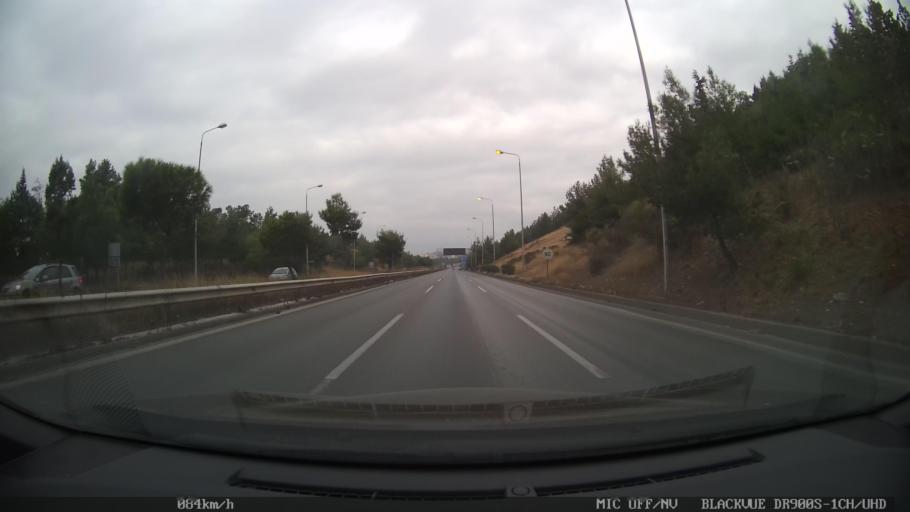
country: GR
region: Central Macedonia
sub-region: Nomos Thessalonikis
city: Agios Pavlos
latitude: 40.6458
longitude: 22.9687
